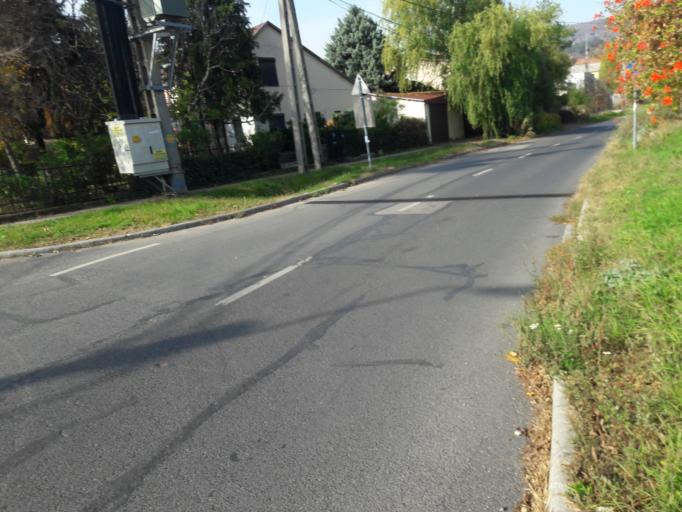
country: HU
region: Pest
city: Budaors
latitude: 47.4628
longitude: 18.9744
